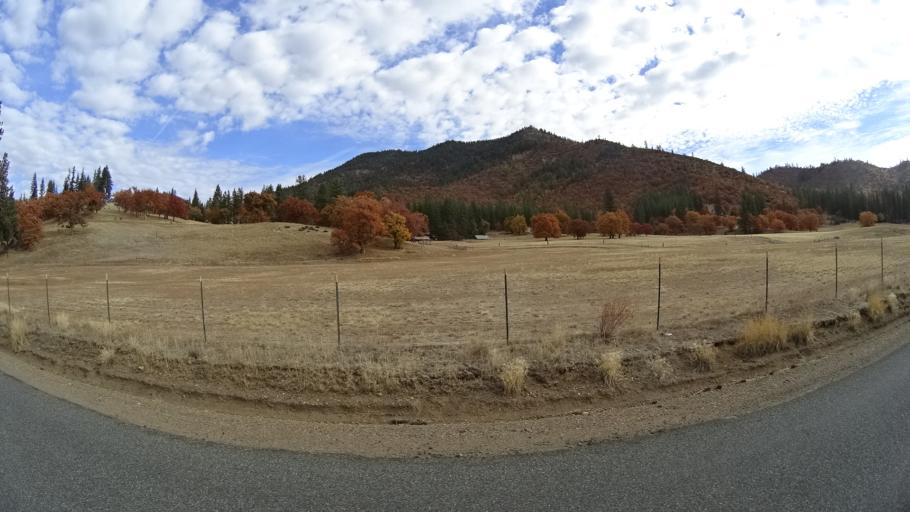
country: US
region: California
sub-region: Siskiyou County
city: Yreka
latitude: 41.6457
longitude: -122.8305
